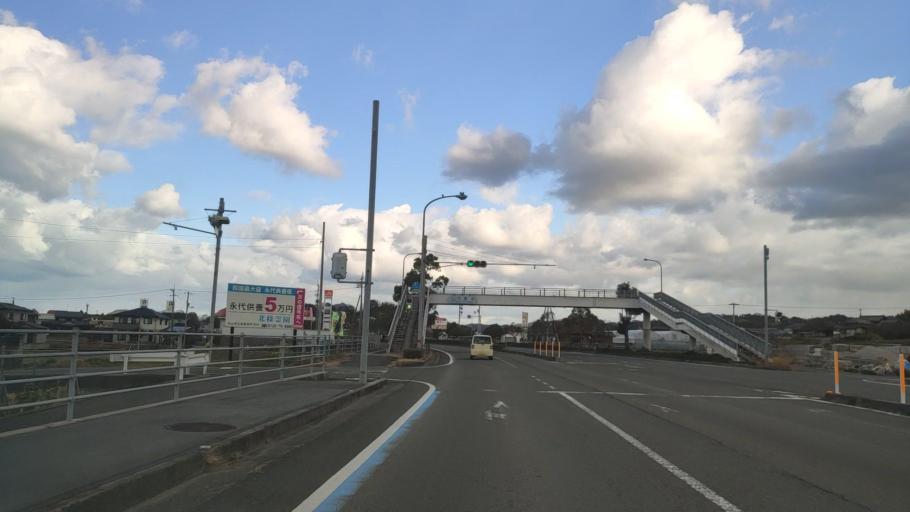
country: JP
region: Ehime
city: Hojo
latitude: 33.9426
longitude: 132.7751
